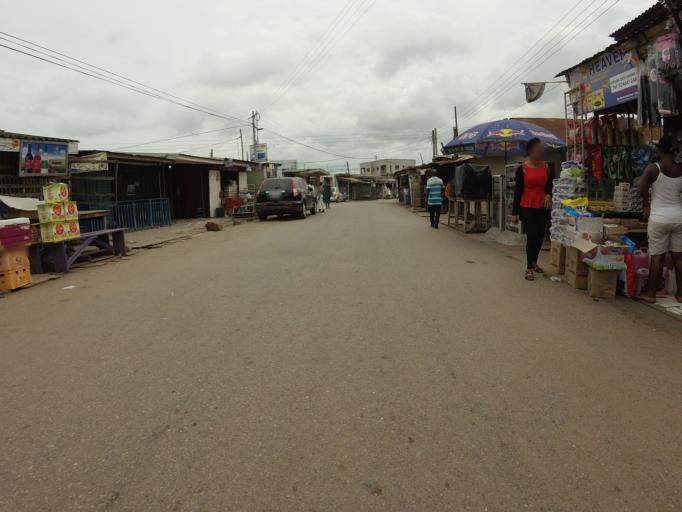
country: GH
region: Greater Accra
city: Accra
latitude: 5.5908
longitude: -0.2163
